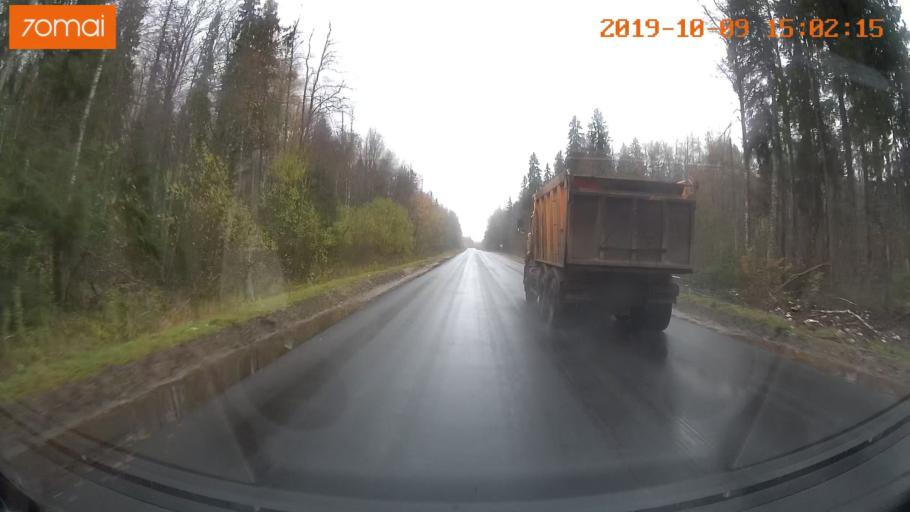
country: RU
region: Kostroma
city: Chistyye Bory
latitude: 58.2879
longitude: 41.6798
